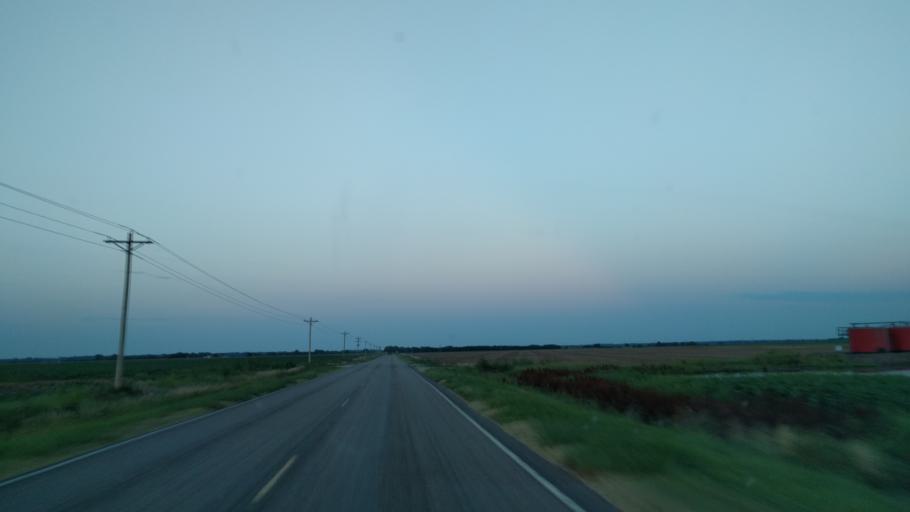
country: US
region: Kansas
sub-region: Reno County
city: Nickerson
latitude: 38.2175
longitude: -98.0978
